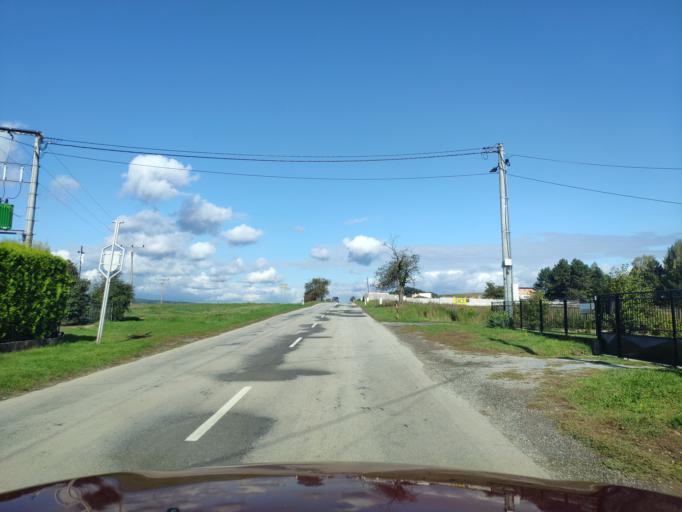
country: SK
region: Presovsky
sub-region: Okres Presov
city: Presov
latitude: 48.8784
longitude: 21.2693
